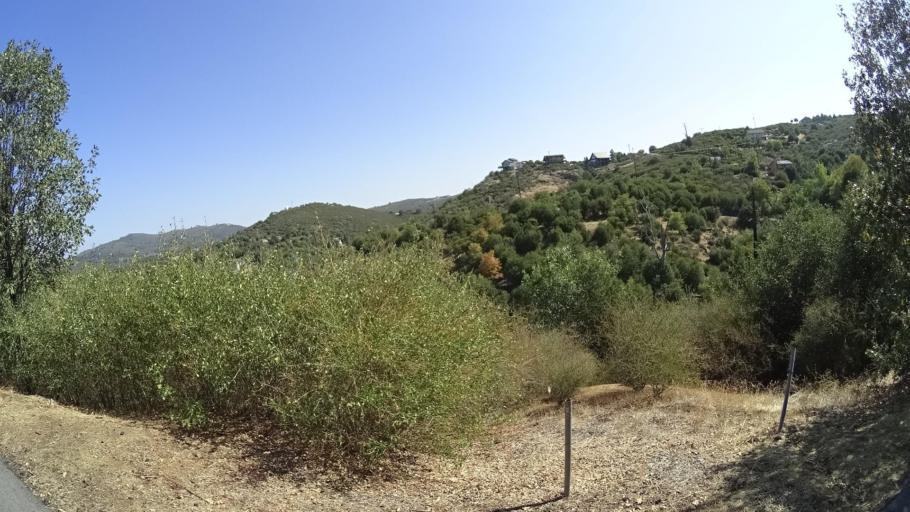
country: US
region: California
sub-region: San Diego County
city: Julian
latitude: 33.0226
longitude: -116.5720
